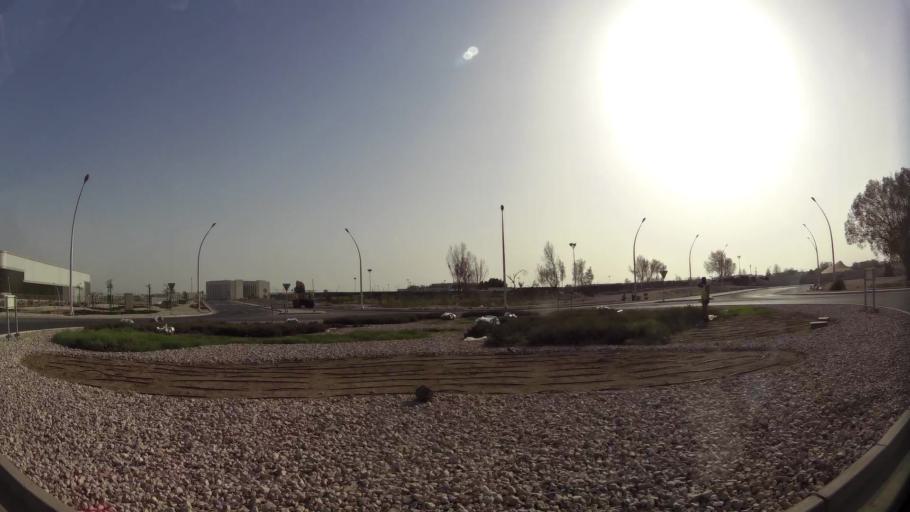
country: QA
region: Baladiyat ar Rayyan
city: Ar Rayyan
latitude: 25.3270
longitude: 51.4304
